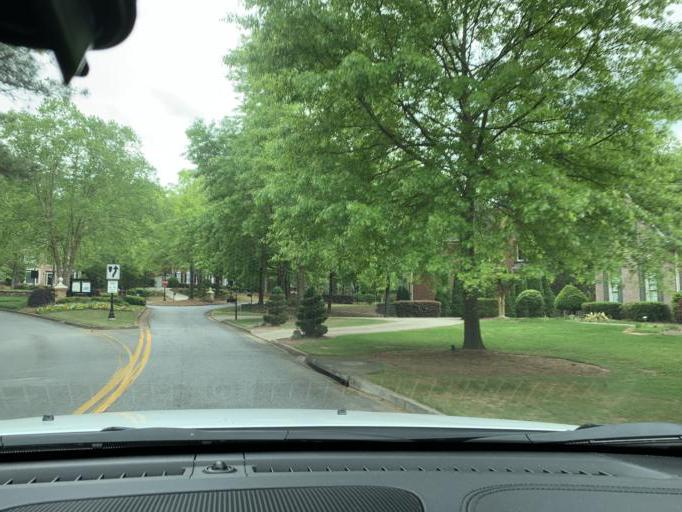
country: US
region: Georgia
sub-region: Gwinnett County
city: Suwanee
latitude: 34.1127
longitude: -84.1124
